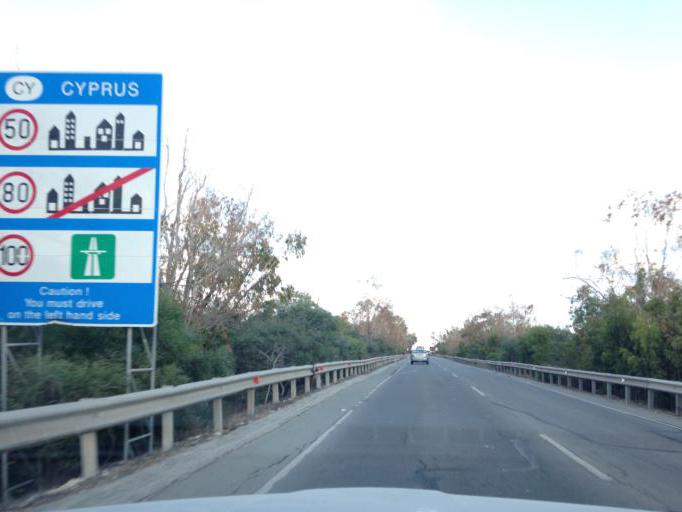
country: CY
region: Pafos
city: Paphos
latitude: 34.7088
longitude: 32.4928
